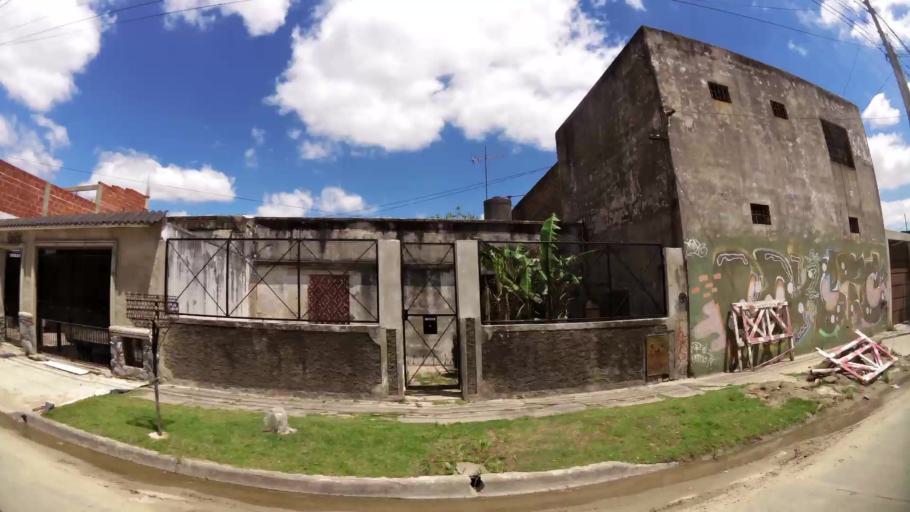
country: AR
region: Buenos Aires
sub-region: Partido de Lanus
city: Lanus
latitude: -34.7048
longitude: -58.4207
